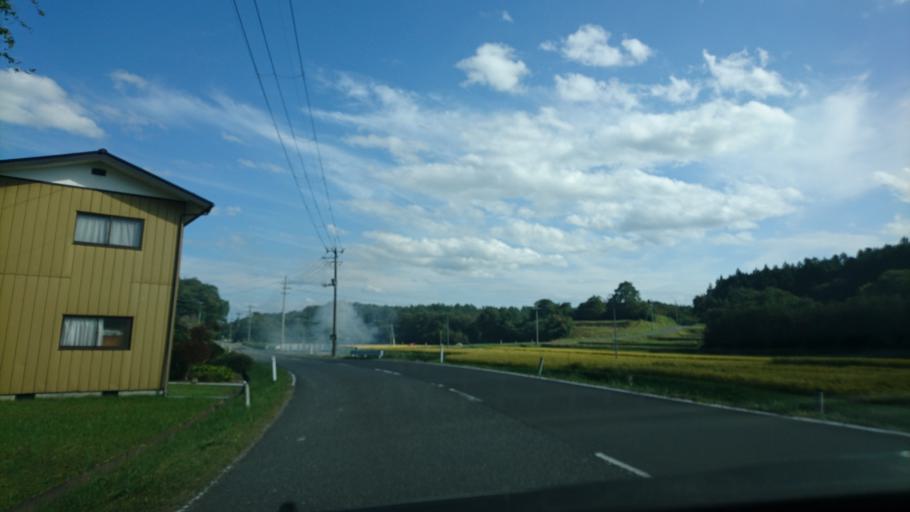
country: JP
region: Iwate
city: Ichinoseki
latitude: 38.8749
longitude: 141.0757
